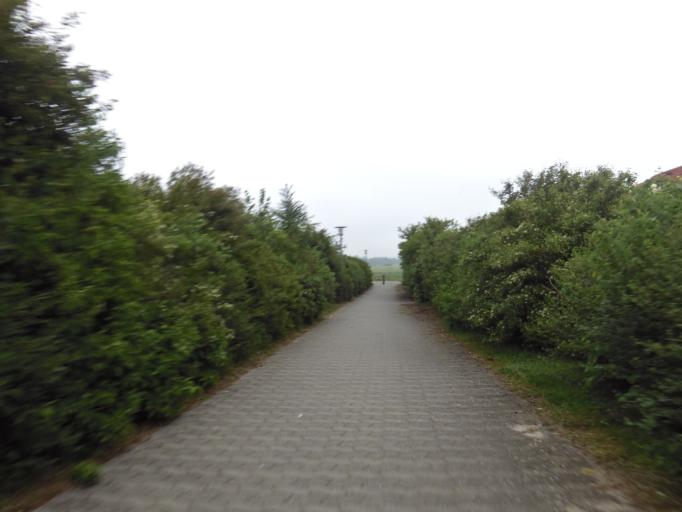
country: DK
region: South Denmark
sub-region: Esbjerg Kommune
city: Ribe
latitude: 55.3254
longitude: 8.7865
